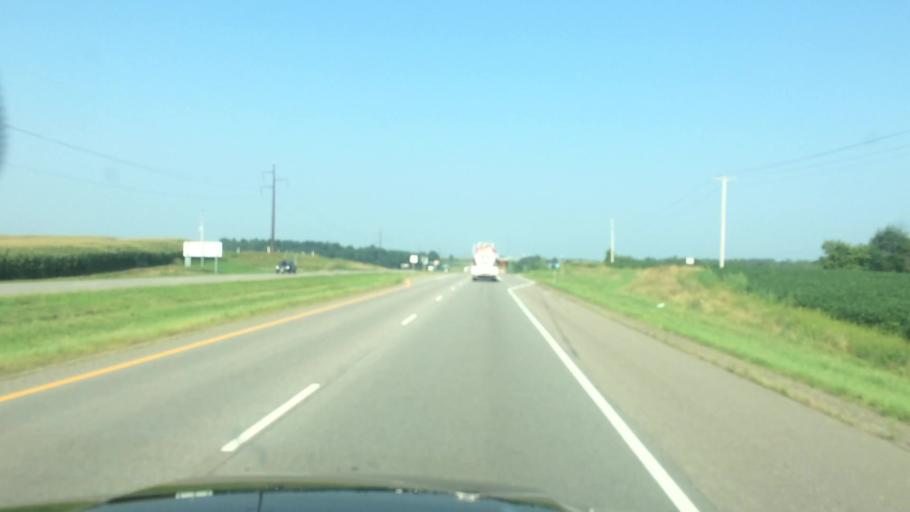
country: US
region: Wisconsin
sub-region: Marathon County
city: Marathon
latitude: 44.9446
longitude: -89.8728
